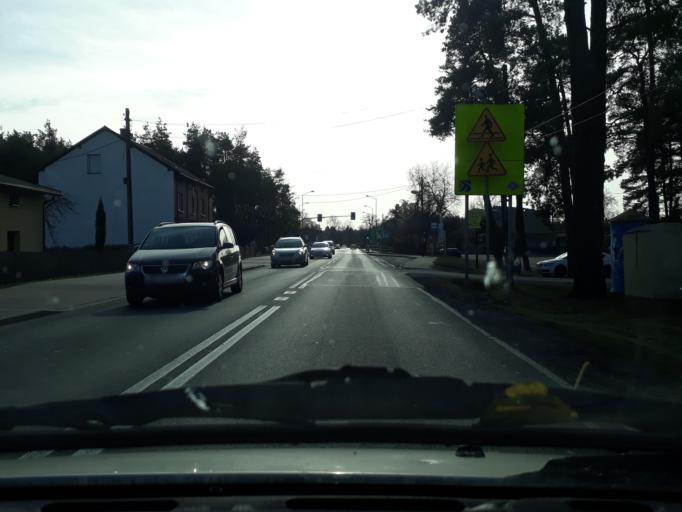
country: PL
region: Silesian Voivodeship
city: Miasteczko Slaskie
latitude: 50.5523
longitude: 18.9566
